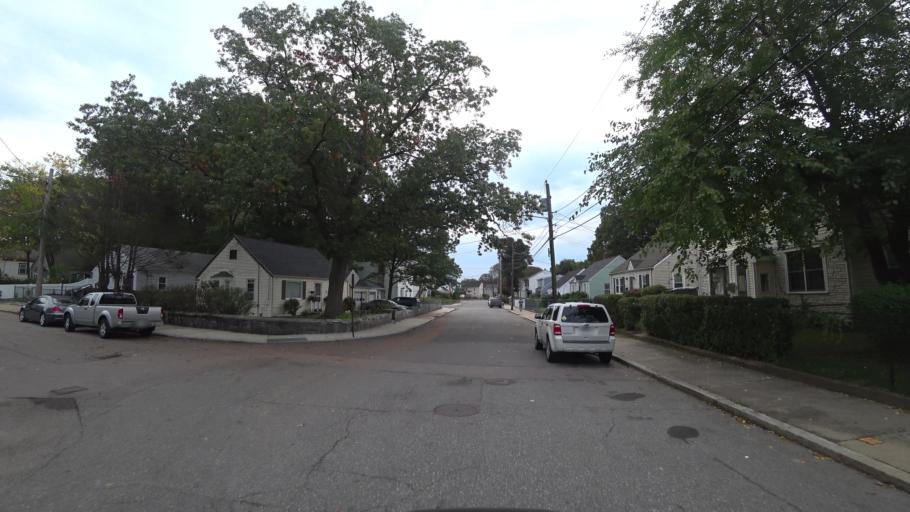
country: US
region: Massachusetts
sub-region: Suffolk County
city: Jamaica Plain
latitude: 42.2668
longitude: -71.1095
